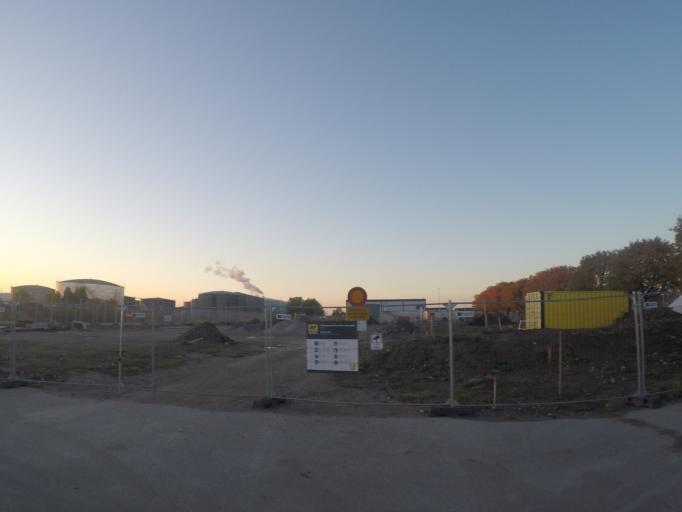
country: SE
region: Skane
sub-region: Burlovs Kommun
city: Arloev
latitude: 55.6328
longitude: 13.0413
